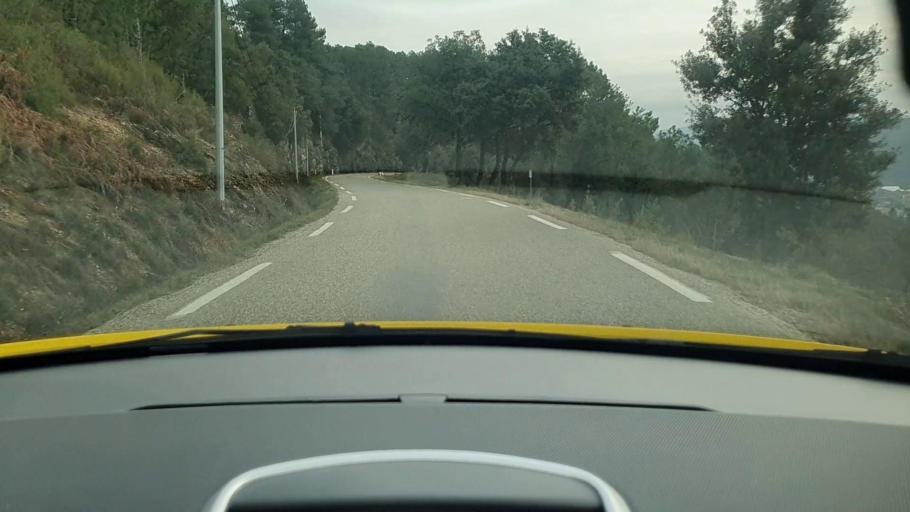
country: FR
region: Languedoc-Roussillon
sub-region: Departement du Gard
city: Besseges
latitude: 44.3097
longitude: 4.0775
